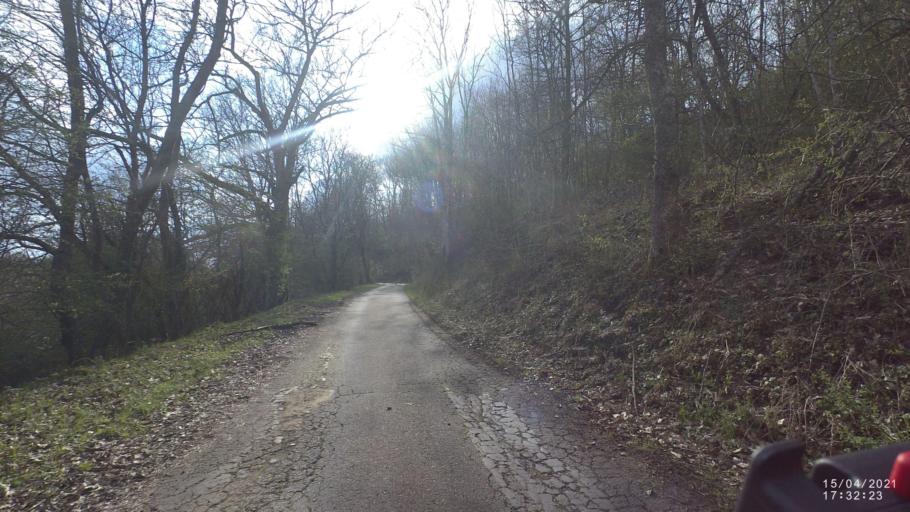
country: DE
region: Rheinland-Pfalz
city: Volkesfeld
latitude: 50.3913
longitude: 7.1606
